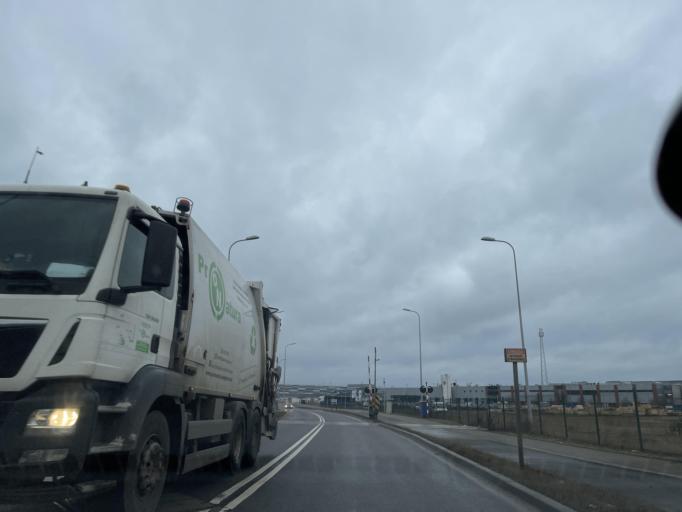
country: PL
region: Kujawsko-Pomorskie
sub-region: Bydgoszcz
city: Bydgoszcz
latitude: 53.0762
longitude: 18.0785
